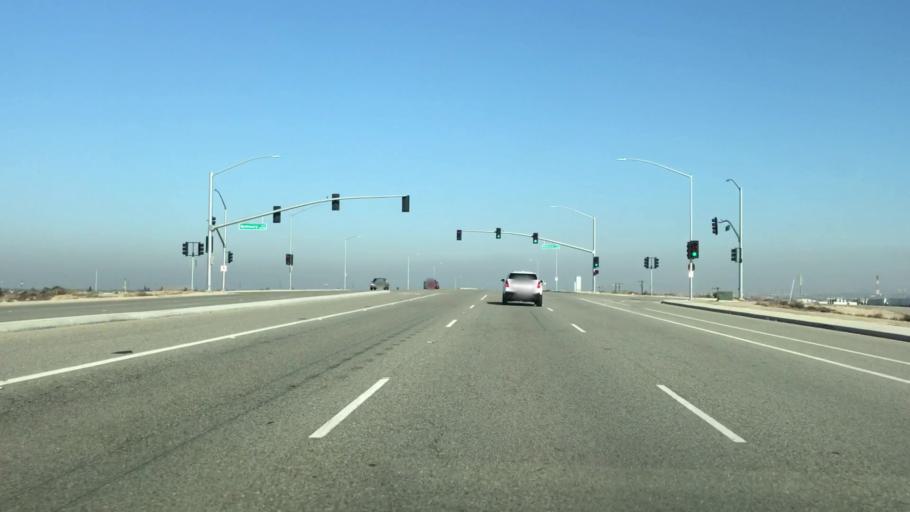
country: US
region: California
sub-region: Kern County
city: Greenacres
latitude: 35.3740
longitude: -119.0659
